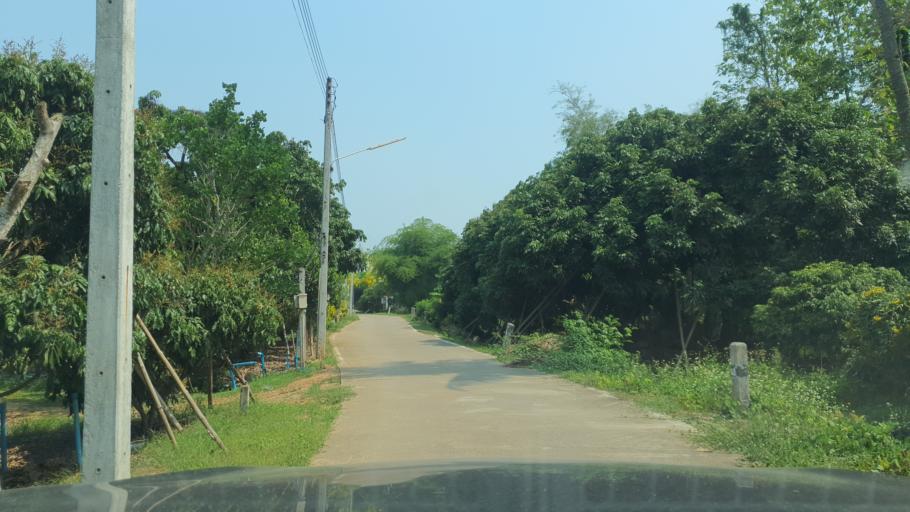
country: TH
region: Chiang Mai
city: Saraphi
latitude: 18.6625
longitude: 98.9888
